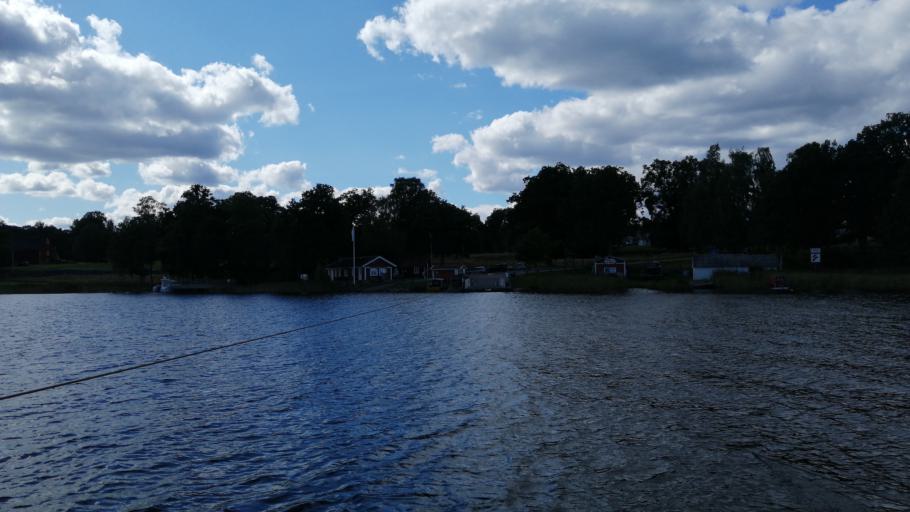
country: SE
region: Joenkoeping
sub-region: Varnamo Kommun
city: Bredaryd
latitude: 57.0092
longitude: 13.7022
